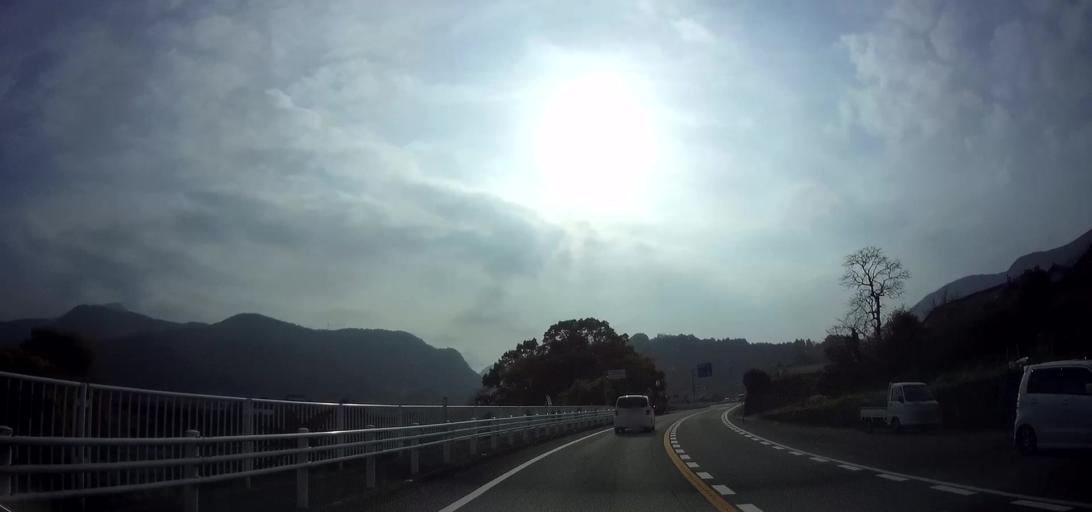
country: JP
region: Nagasaki
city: Shimabara
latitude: 32.7838
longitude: 130.2048
